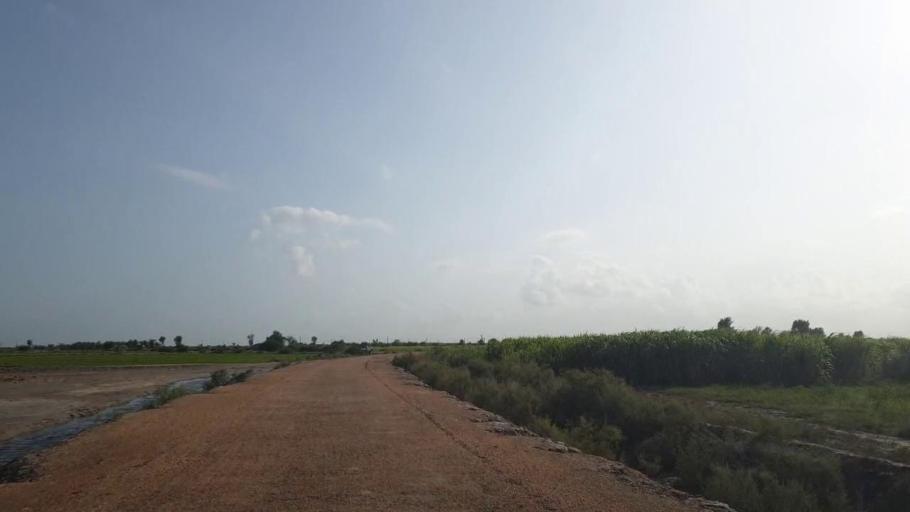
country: PK
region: Sindh
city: Kadhan
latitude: 24.6096
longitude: 69.0894
